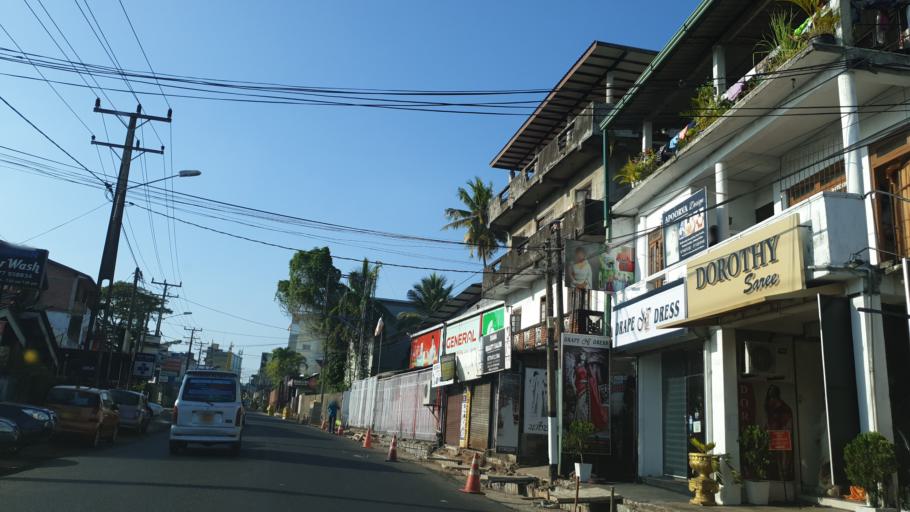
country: LK
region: Western
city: Sri Jayewardenepura Kotte
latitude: 6.8704
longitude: 79.9071
